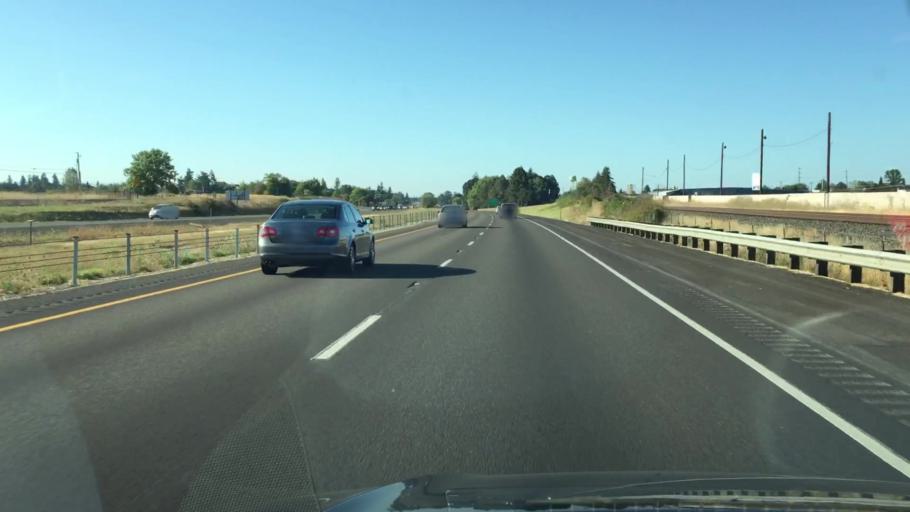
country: US
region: Oregon
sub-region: Linn County
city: Millersburg
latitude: 44.6724
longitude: -123.0580
